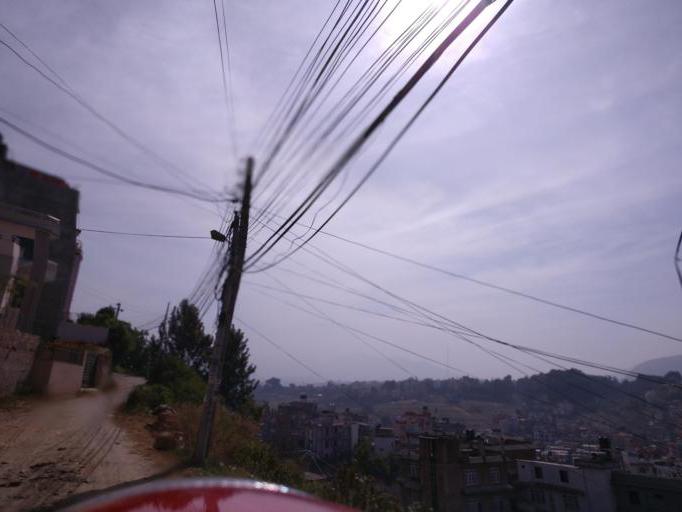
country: NP
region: Central Region
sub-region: Bagmati Zone
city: Patan
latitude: 27.6603
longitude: 85.3111
